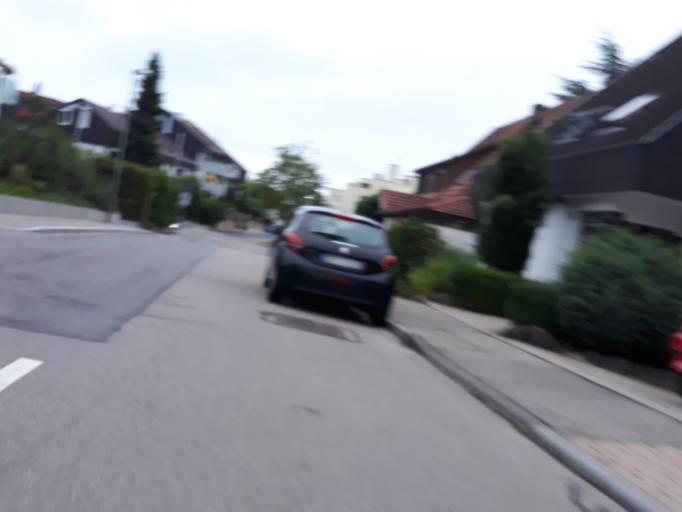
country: DE
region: Baden-Wuerttemberg
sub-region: Regierungsbezirk Stuttgart
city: Schonaich
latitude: 48.6652
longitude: 9.0586
